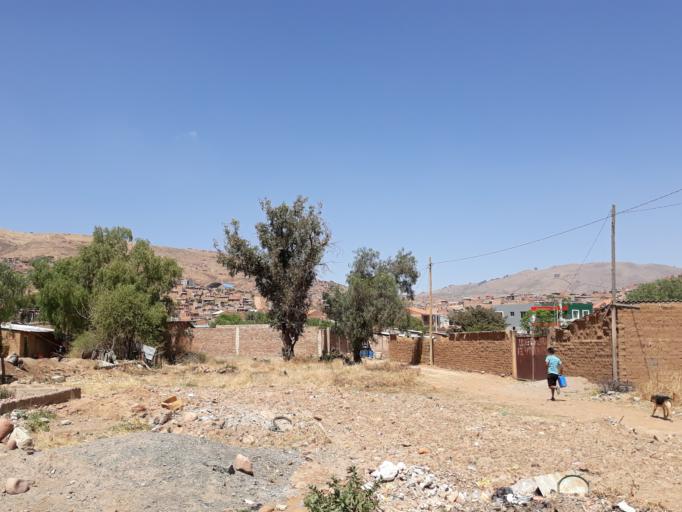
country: BO
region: Cochabamba
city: Cochabamba
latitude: -17.4661
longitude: -66.1387
